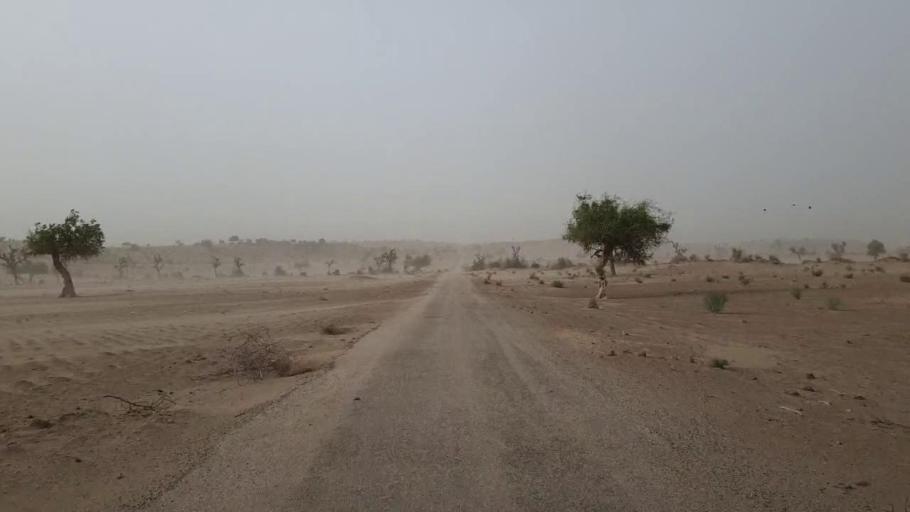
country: PK
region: Sindh
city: Islamkot
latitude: 24.5499
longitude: 70.3600
